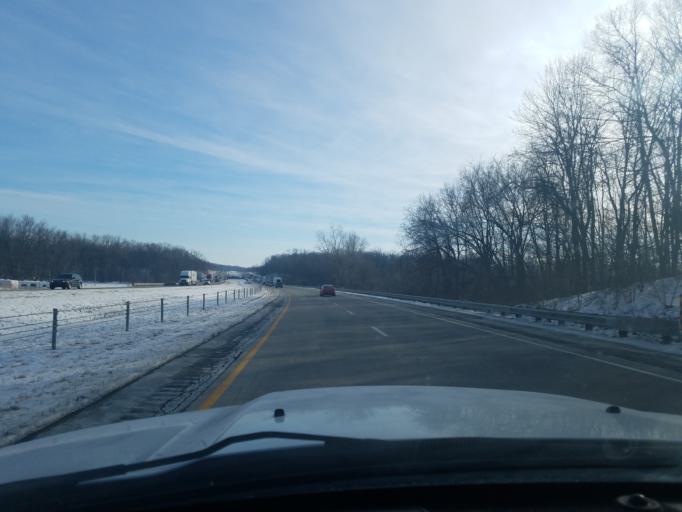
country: US
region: Indiana
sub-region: Grant County
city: Upland
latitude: 40.4586
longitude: -85.5514
